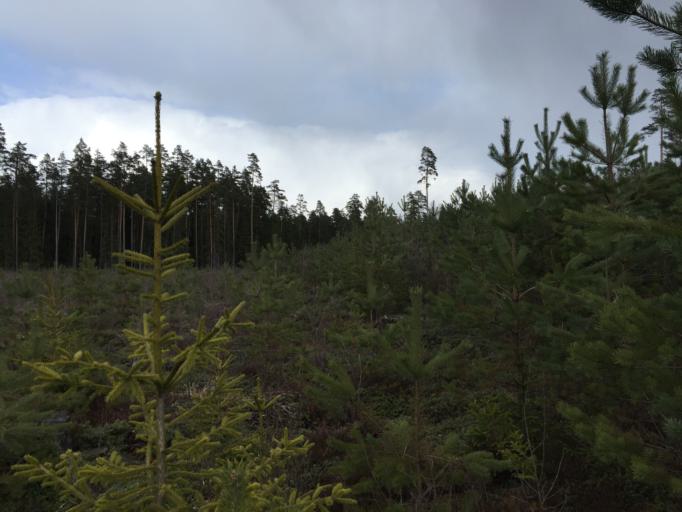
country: LV
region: Garkalne
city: Garkalne
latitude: 56.9593
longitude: 24.4923
